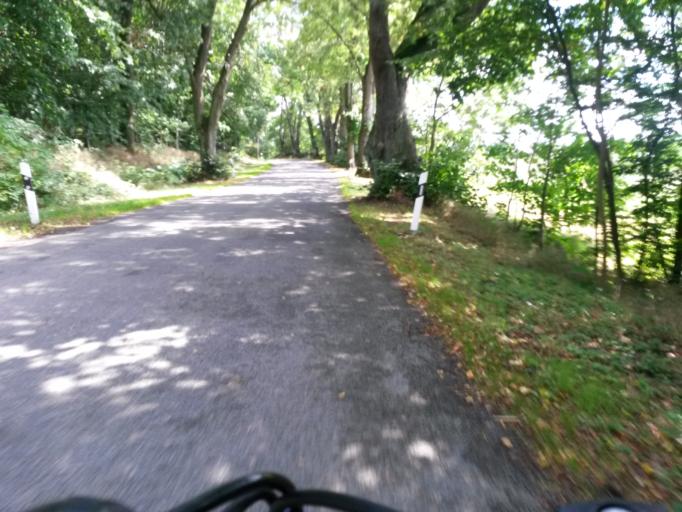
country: DE
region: Brandenburg
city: Angermunde
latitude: 53.0075
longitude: 13.9312
